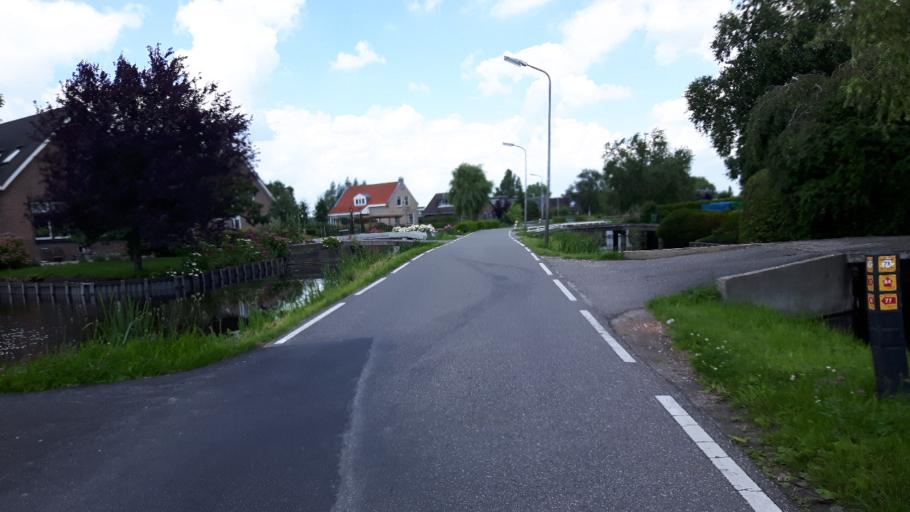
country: NL
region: South Holland
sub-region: Gemeente Gouda
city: Bloemendaal
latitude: 52.0360
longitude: 4.6899
